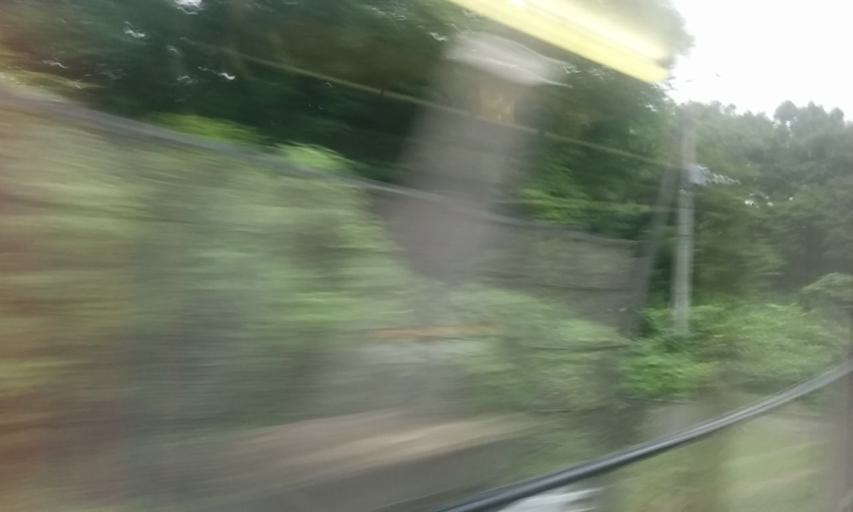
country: JP
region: Tochigi
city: Kuroiso
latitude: 37.0000
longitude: 140.0850
